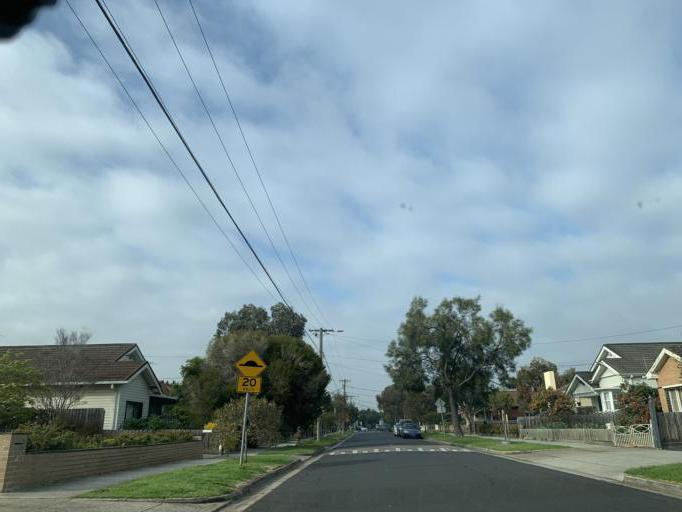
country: AU
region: Victoria
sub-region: Moreland
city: Pascoe Vale South
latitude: -37.7371
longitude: 144.9445
